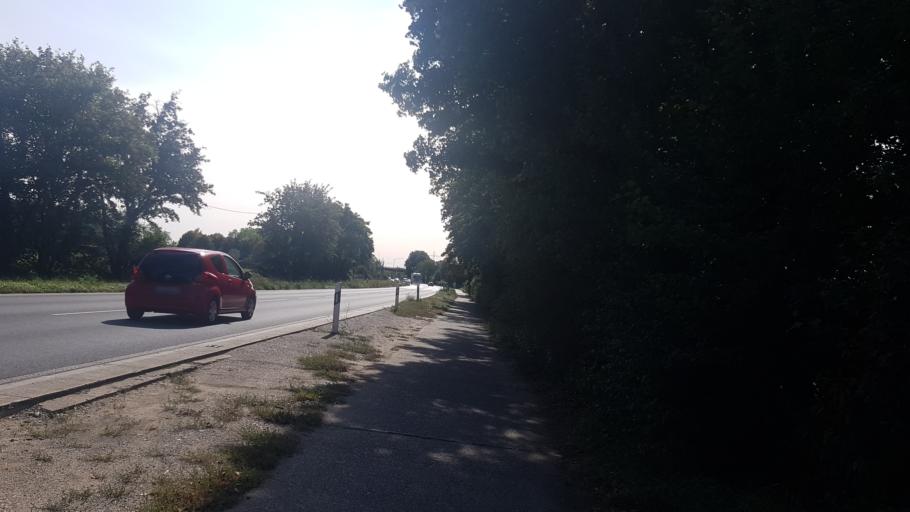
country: DE
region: North Rhine-Westphalia
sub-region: Regierungsbezirk Dusseldorf
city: Ratingen
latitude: 51.3172
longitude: 6.8316
